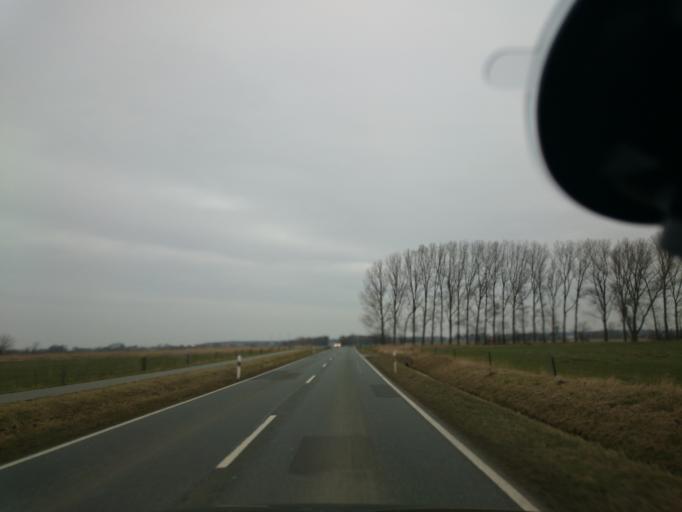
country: DE
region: Mecklenburg-Vorpommern
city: Borgerende-Rethwisch
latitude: 54.1284
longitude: 11.9262
